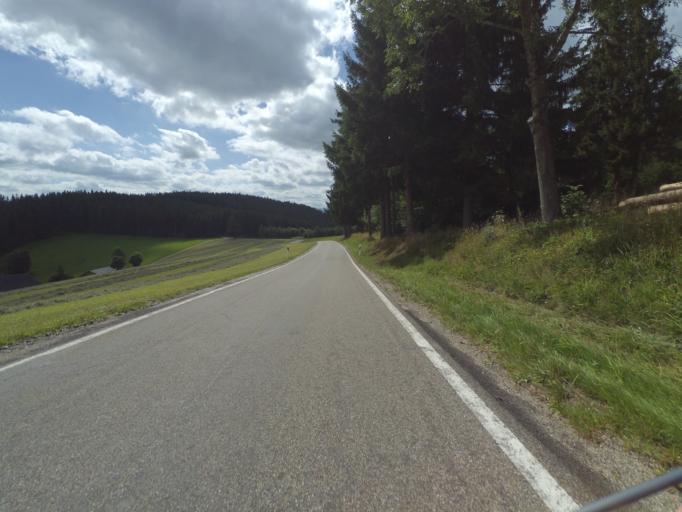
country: DE
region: Baden-Wuerttemberg
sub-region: Freiburg Region
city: Friedenweiler
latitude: 47.9454
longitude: 8.2261
